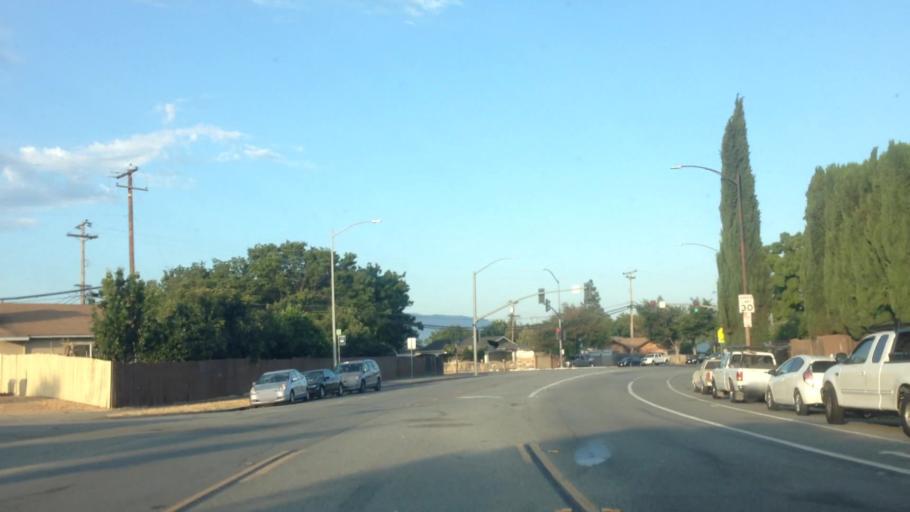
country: US
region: California
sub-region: Santa Clara County
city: Seven Trees
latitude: 37.2886
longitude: -121.8206
